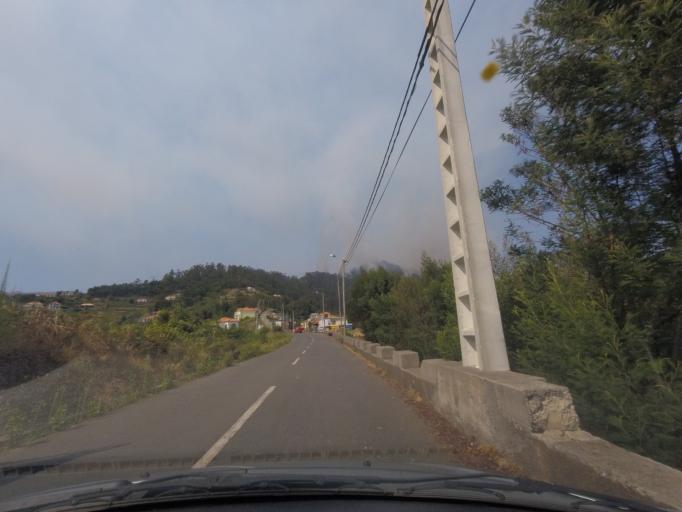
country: PT
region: Madeira
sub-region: Ribeira Brava
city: Campanario
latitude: 32.6912
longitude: -17.0570
